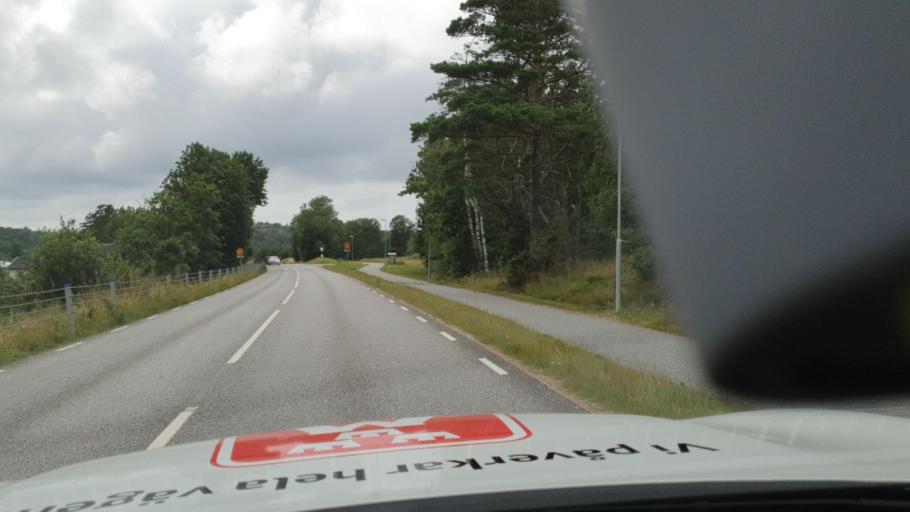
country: SE
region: Vaestra Goetaland
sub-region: Tanums Kommun
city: Tanumshede
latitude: 58.7216
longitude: 11.3061
